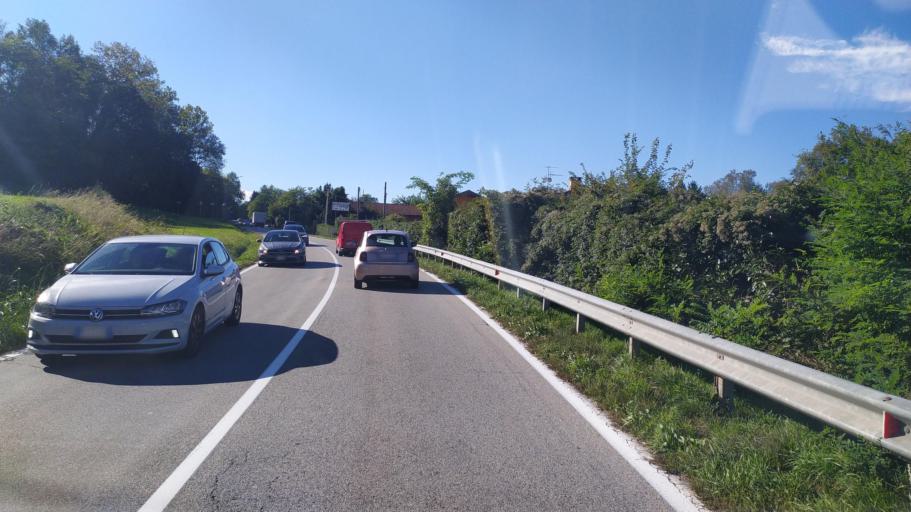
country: IT
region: Lombardy
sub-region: Provincia di Varese
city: Galliate Lombardo
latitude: 45.7905
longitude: 8.7672
